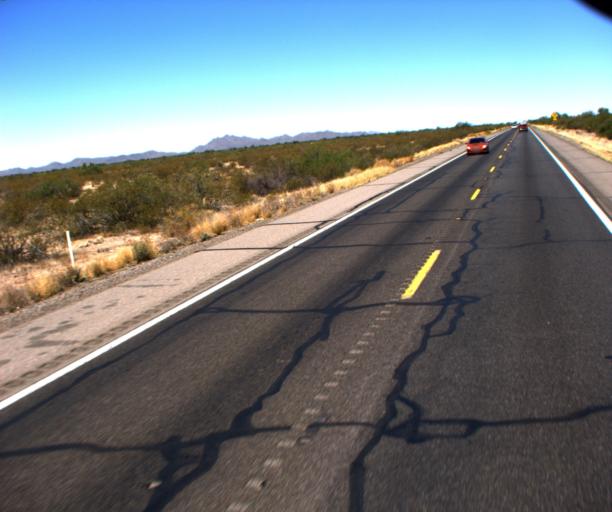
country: US
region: Arizona
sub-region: Yavapai County
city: Congress
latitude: 34.0489
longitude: -112.8435
